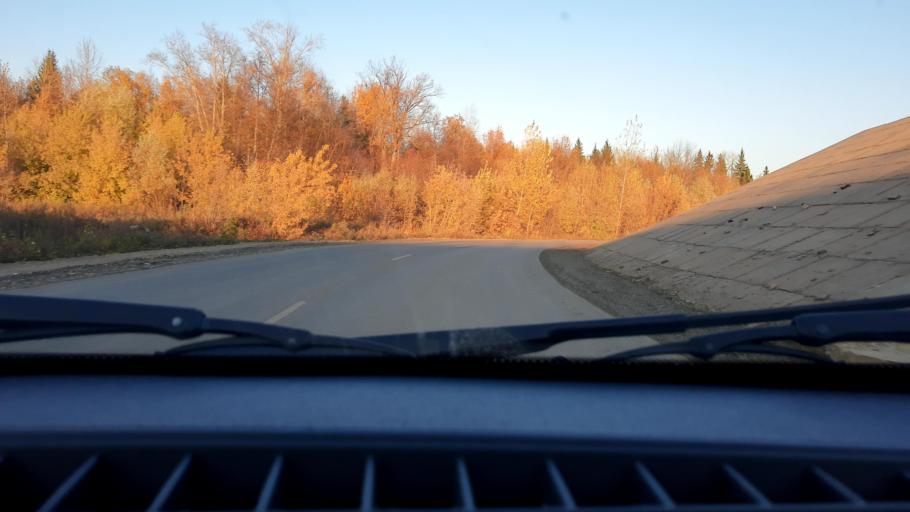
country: RU
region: Bashkortostan
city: Ufa
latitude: 54.6823
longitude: 56.0047
